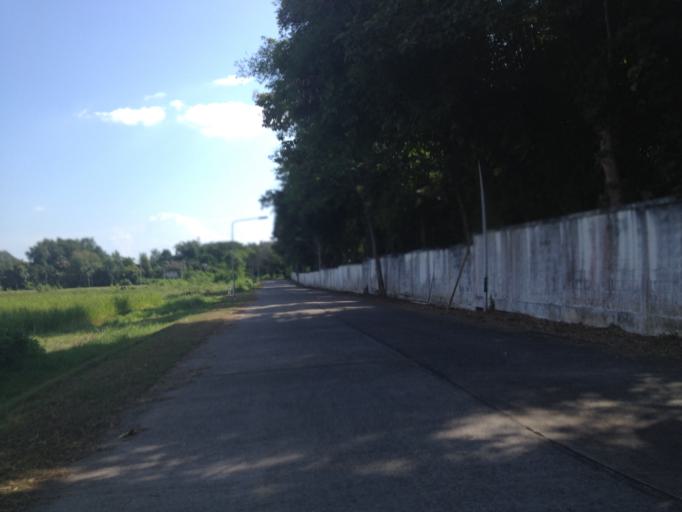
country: TH
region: Chiang Mai
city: Chiang Mai
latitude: 18.7611
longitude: 98.9272
